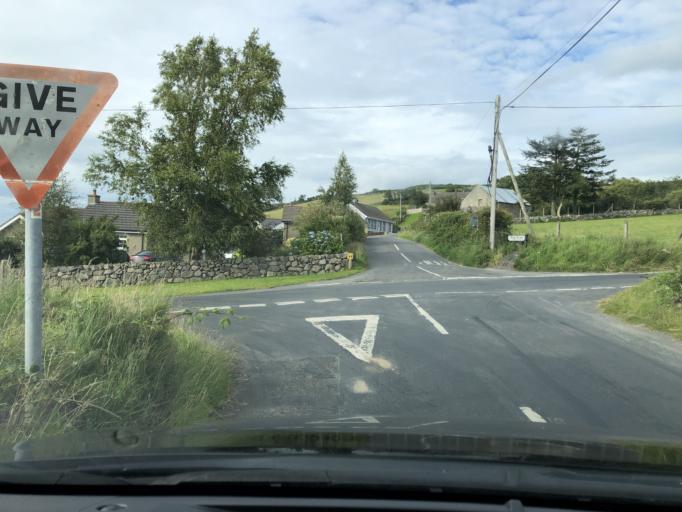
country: GB
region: Northern Ireland
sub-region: Down District
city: Castlewellan
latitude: 54.2292
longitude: -6.0114
